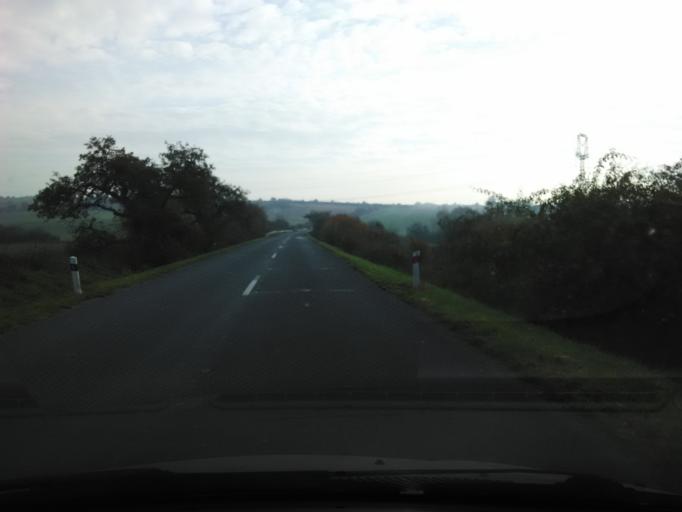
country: SK
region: Nitriansky
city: Levice
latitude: 48.2896
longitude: 18.6689
